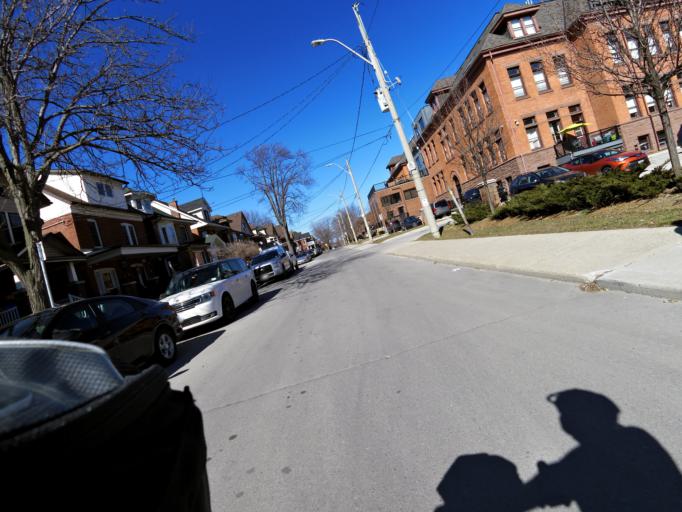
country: CA
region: Ontario
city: Hamilton
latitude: 43.2466
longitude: -79.8533
